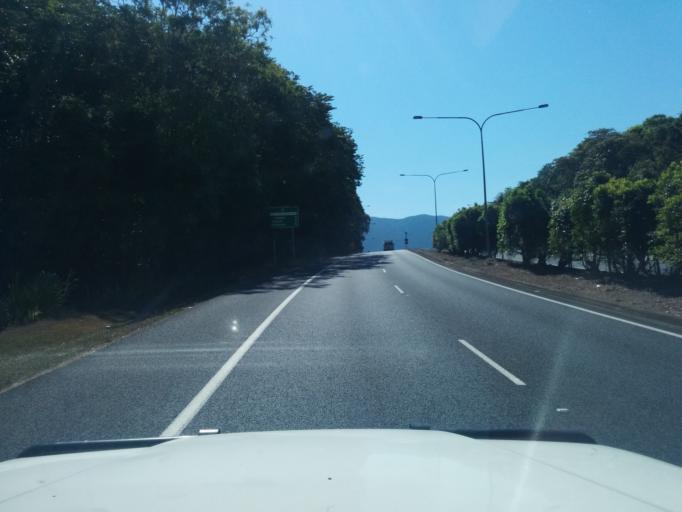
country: AU
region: Queensland
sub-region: Cairns
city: Redlynch
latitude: -16.9144
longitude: 145.7251
